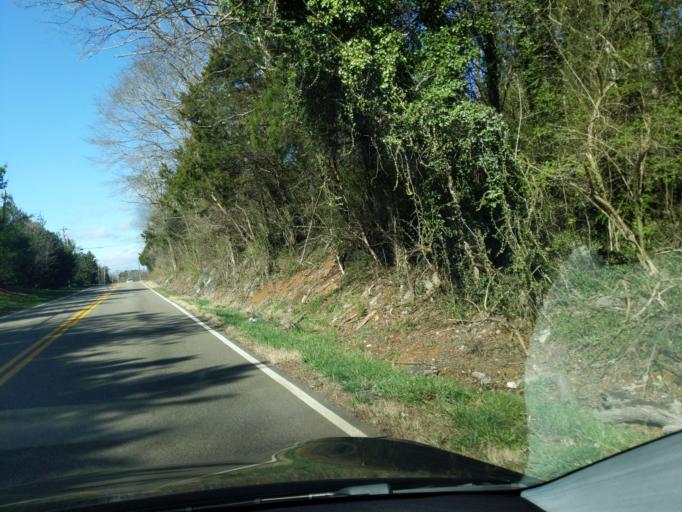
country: US
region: Tennessee
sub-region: Jefferson County
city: Dandridge
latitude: 35.9763
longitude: -83.4879
